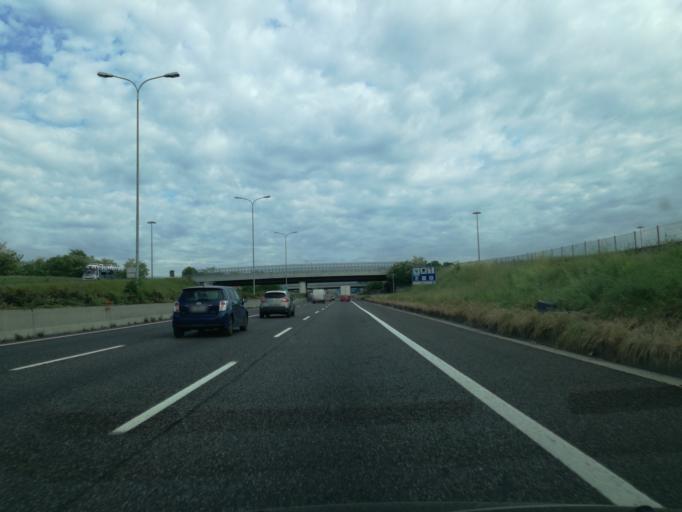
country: IT
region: Lombardy
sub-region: Provincia di Monza e Brianza
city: Carate Brianza
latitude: 45.6636
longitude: 9.2236
